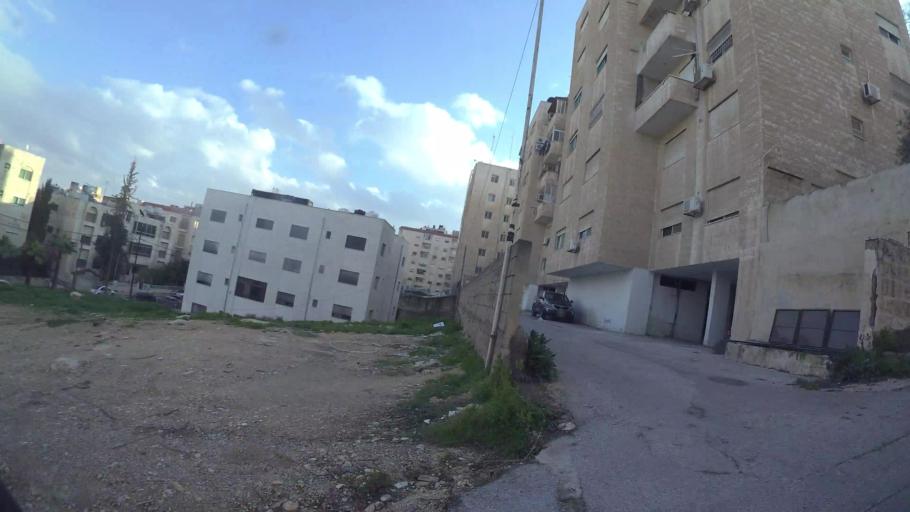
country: JO
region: Amman
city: Al Jubayhah
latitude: 31.9982
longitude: 35.8694
